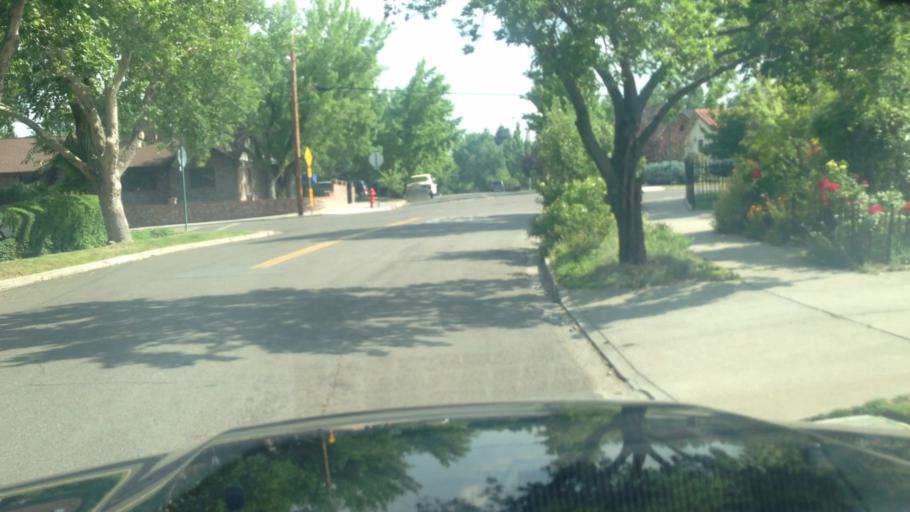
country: US
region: Nevada
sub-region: Washoe County
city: Reno
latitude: 39.5152
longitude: -119.8225
